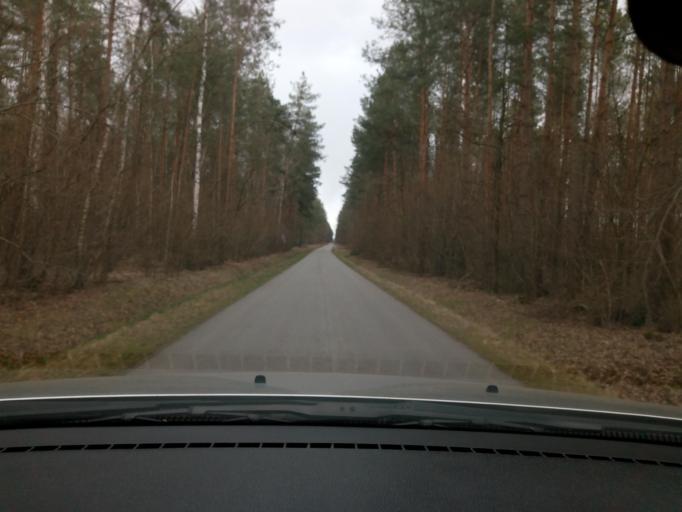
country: PL
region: Swietokrzyskie
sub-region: Powiat starachowicki
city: Brody
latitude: 51.0695
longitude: 21.3084
